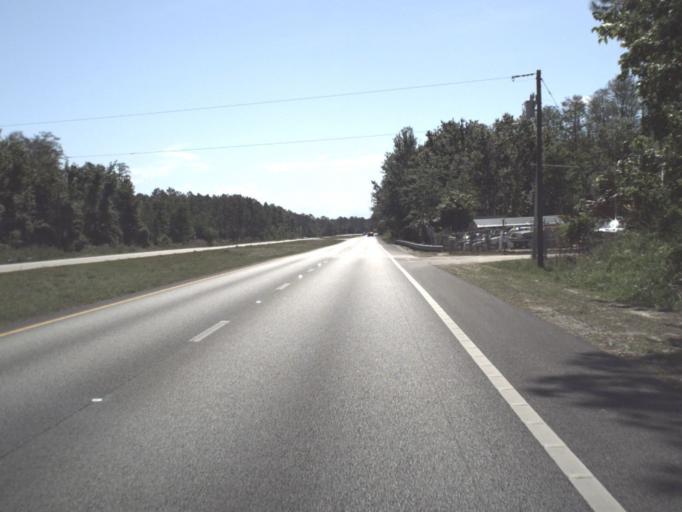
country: US
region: Florida
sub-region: Flagler County
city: Bunnell
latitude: 29.4243
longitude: -81.2186
